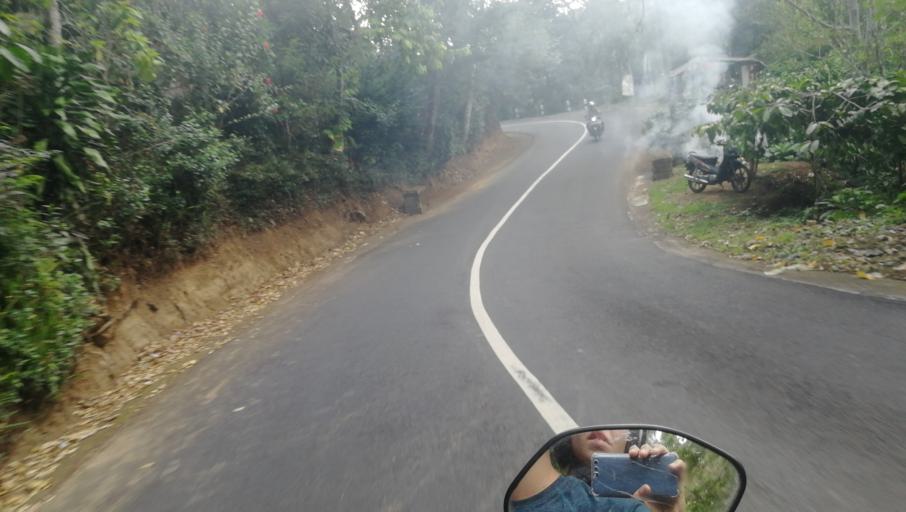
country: ID
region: Bali
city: Munduk
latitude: -8.2561
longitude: 115.0738
